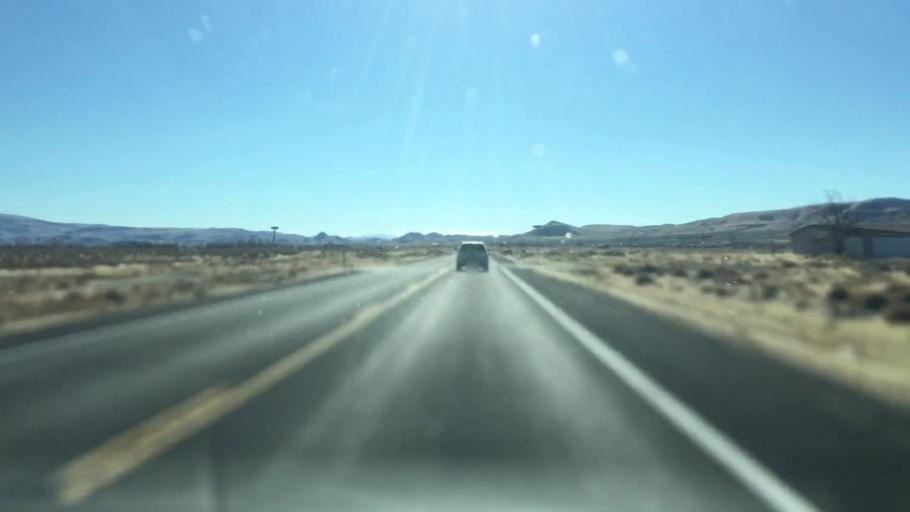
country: US
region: Nevada
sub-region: Lyon County
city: Silver Springs
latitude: 39.3832
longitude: -119.2320
